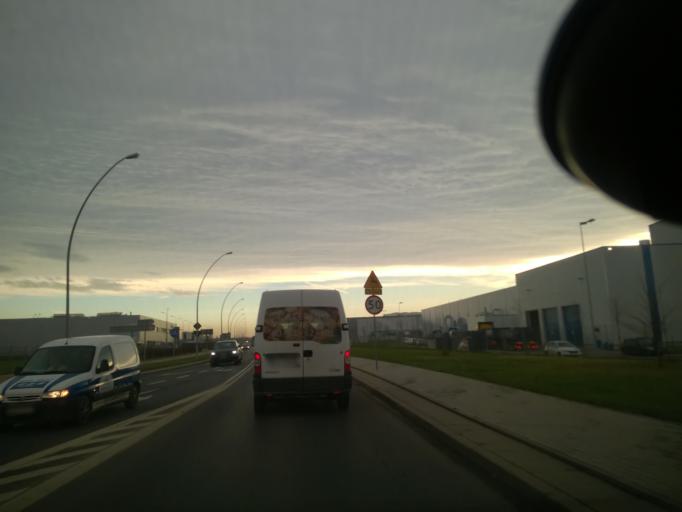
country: PL
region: Lower Silesian Voivodeship
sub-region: Powiat wroclawski
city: Bielany Wroclawskie
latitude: 51.0758
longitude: 16.9501
